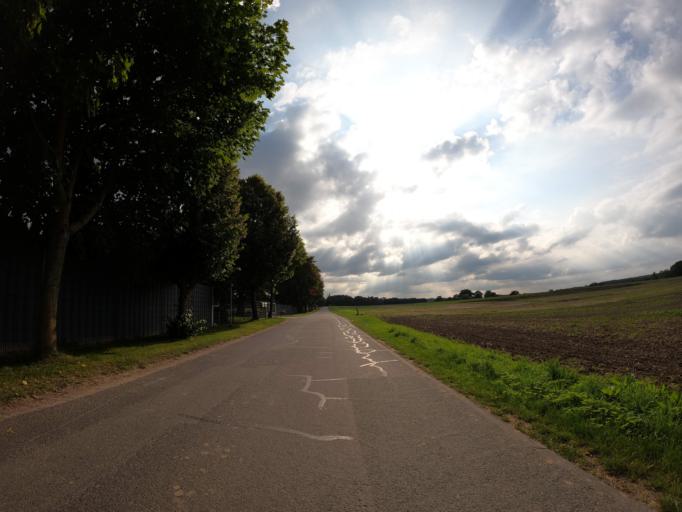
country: DE
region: Mecklenburg-Vorpommern
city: Robel
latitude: 53.4369
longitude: 12.5464
